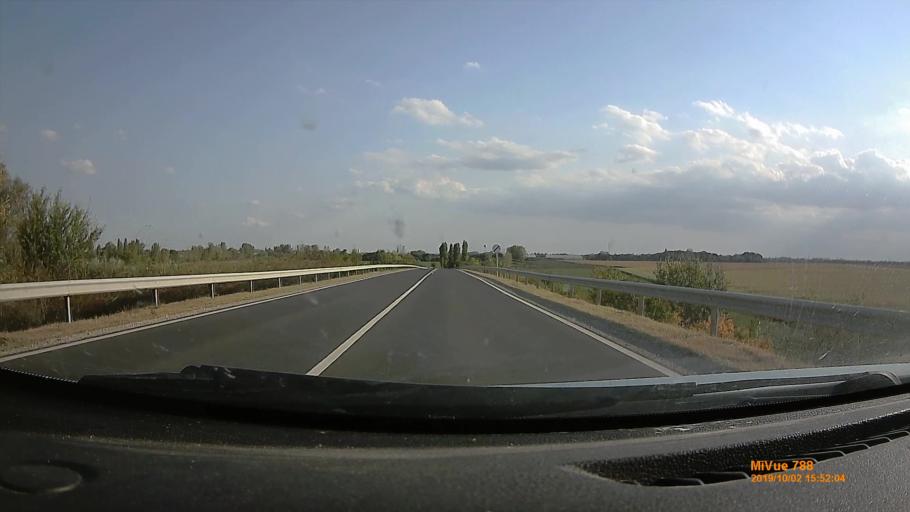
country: HU
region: Heves
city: Fuzesabony
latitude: 47.7474
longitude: 20.3991
